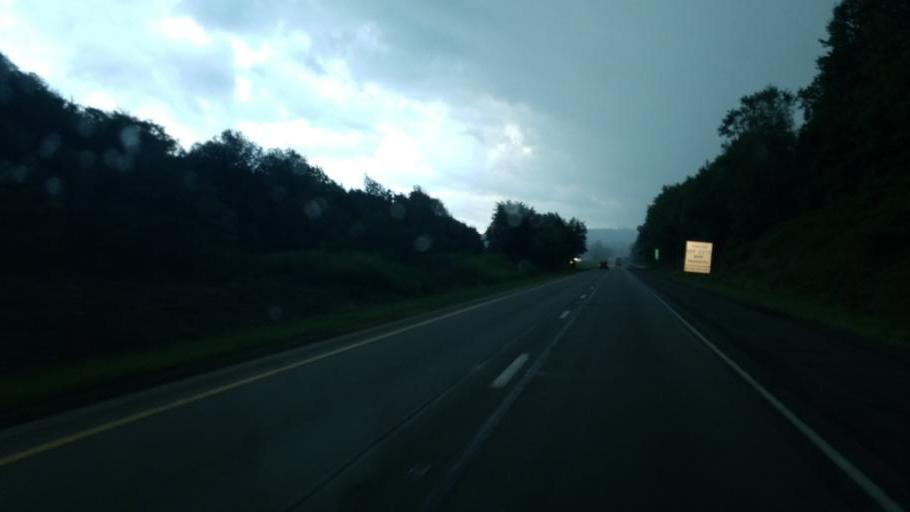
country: US
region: Pennsylvania
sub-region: Butler County
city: Prospect
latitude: 40.9357
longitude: -80.1340
